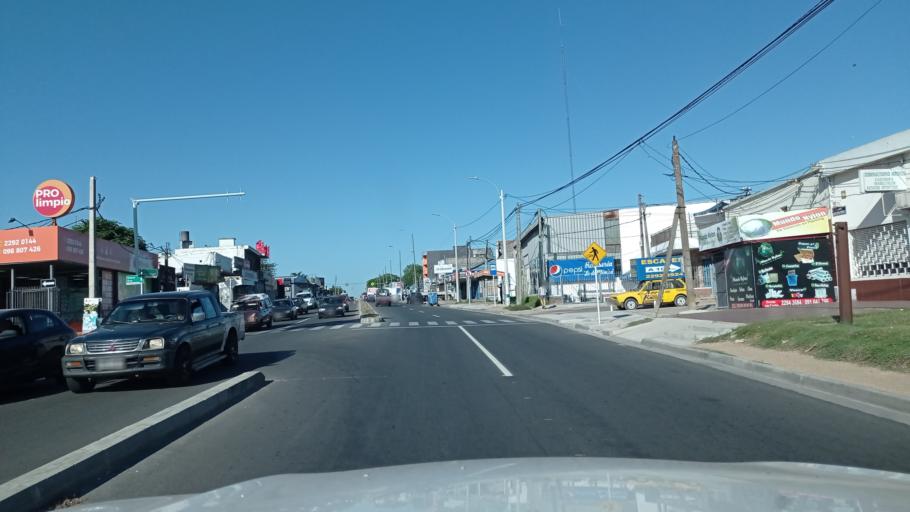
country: UY
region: Canelones
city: Pando
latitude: -34.7251
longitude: -55.9609
